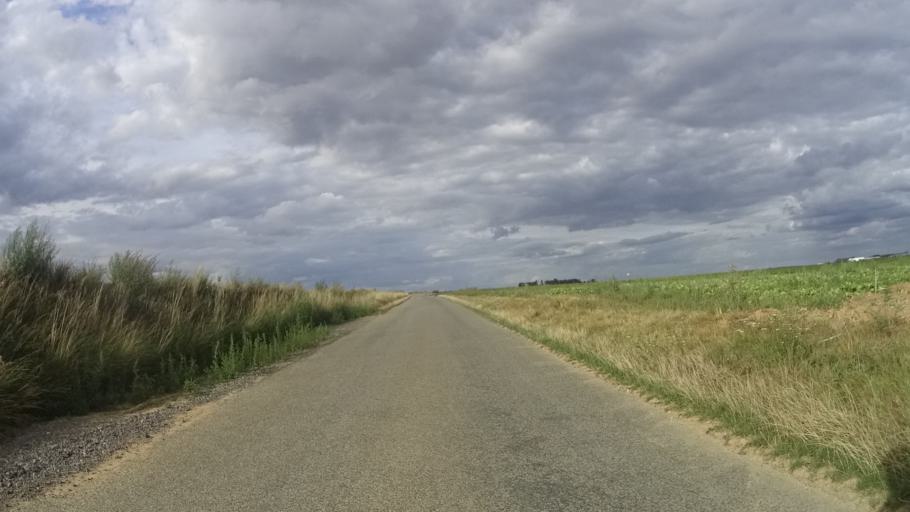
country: FR
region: Picardie
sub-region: Departement de l'Oise
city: Ver-sur-Launette
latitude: 49.0973
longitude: 2.7130
